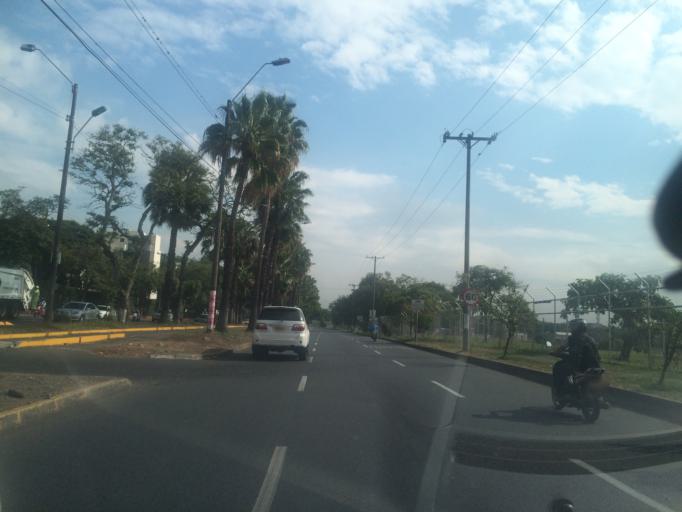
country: CO
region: Valle del Cauca
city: Cali
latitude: 3.3760
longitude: -76.5373
